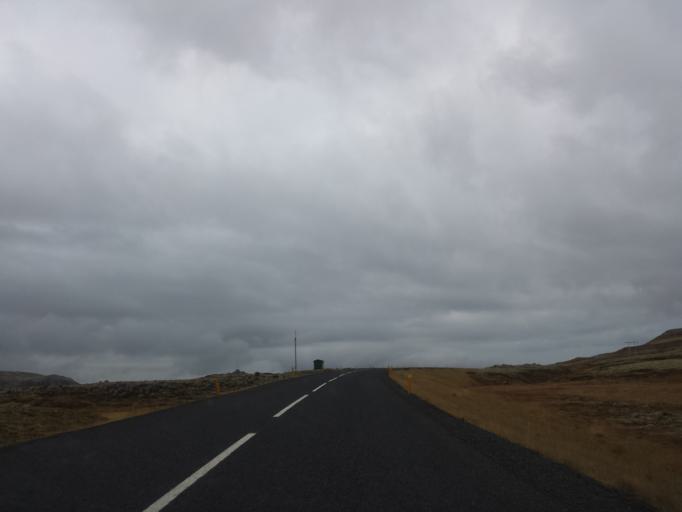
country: IS
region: West
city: Stykkisholmur
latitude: 64.9064
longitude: -22.8598
